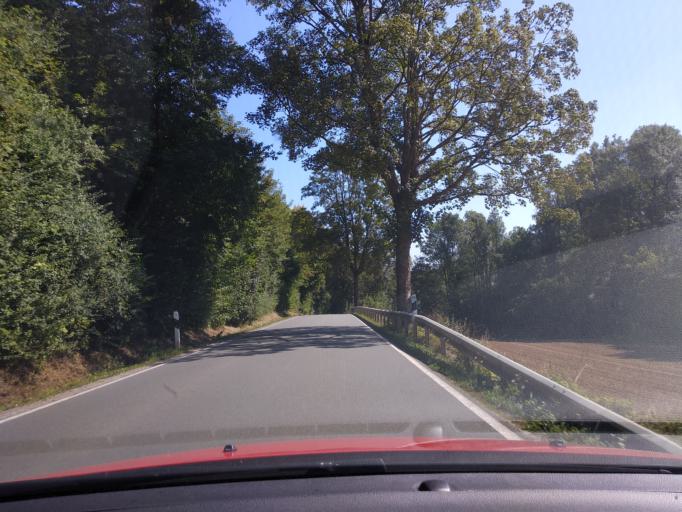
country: DE
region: North Rhine-Westphalia
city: Beverungen
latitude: 51.6785
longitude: 9.3518
